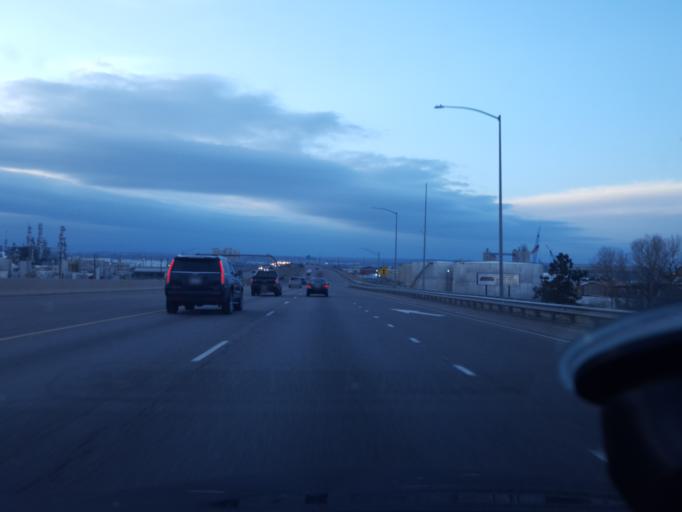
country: US
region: Colorado
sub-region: Adams County
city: Commerce City
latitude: 39.8007
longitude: -104.9337
